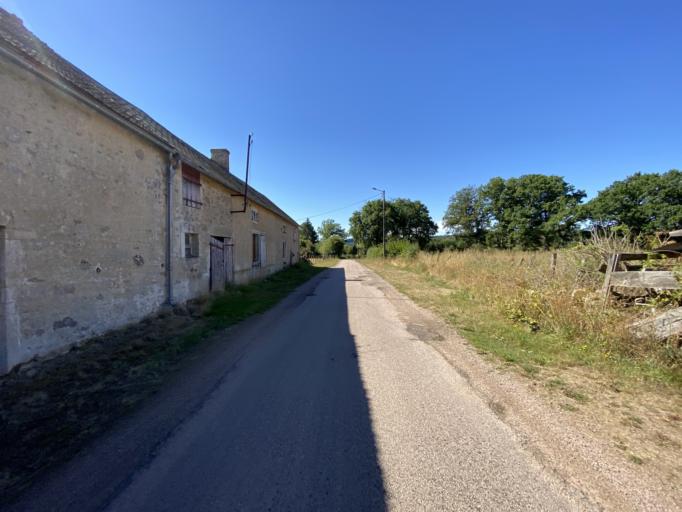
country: FR
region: Bourgogne
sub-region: Departement de la Cote-d'Or
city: Saulieu
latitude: 47.2770
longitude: 4.1790
